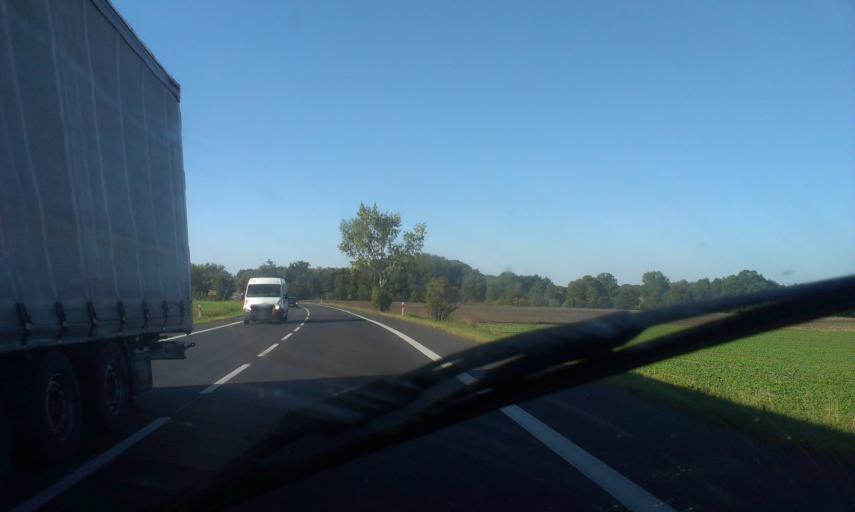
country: PL
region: Kujawsko-Pomorskie
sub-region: Powiat torunski
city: Chelmza
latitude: 53.2029
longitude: 18.5654
